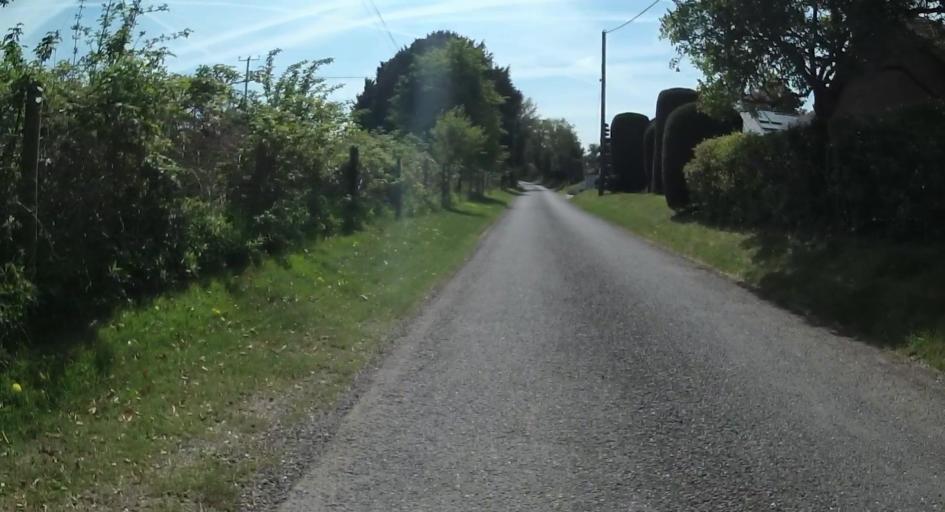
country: GB
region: England
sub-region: Hampshire
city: Chandlers Ford
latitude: 51.0869
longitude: -1.4314
